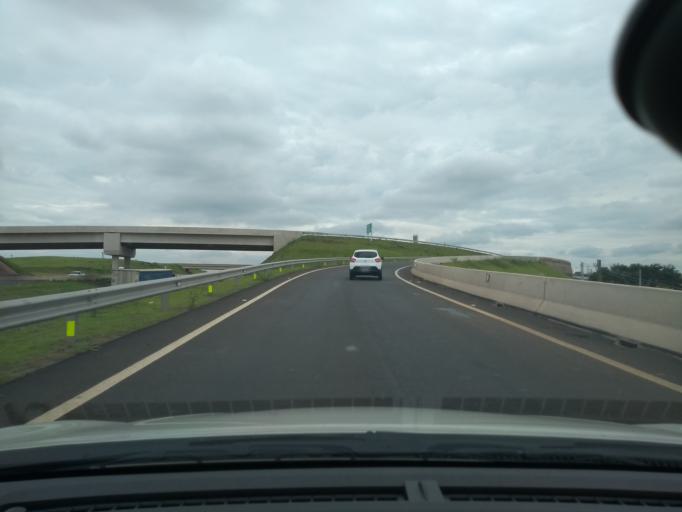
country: BR
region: Sao Paulo
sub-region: Araras
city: Araras
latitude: -22.3797
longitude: -47.3941
